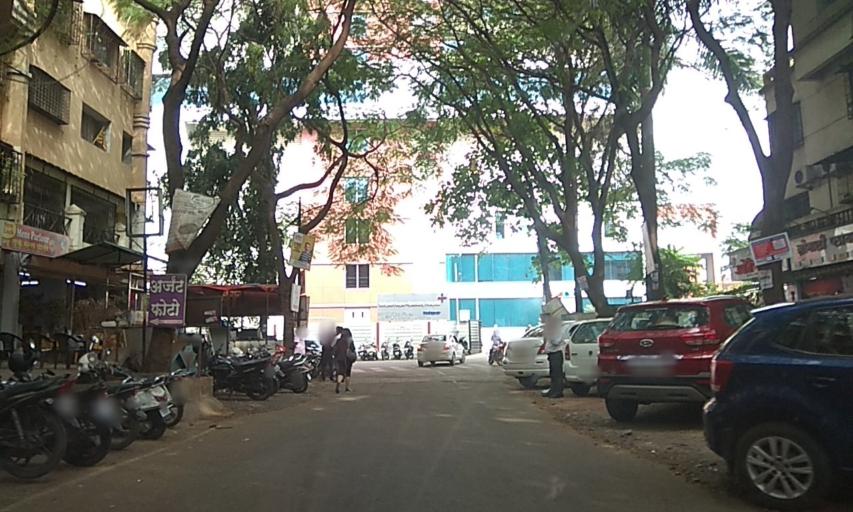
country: IN
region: Maharashtra
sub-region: Pune Division
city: Pune
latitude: 18.5026
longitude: 73.9320
